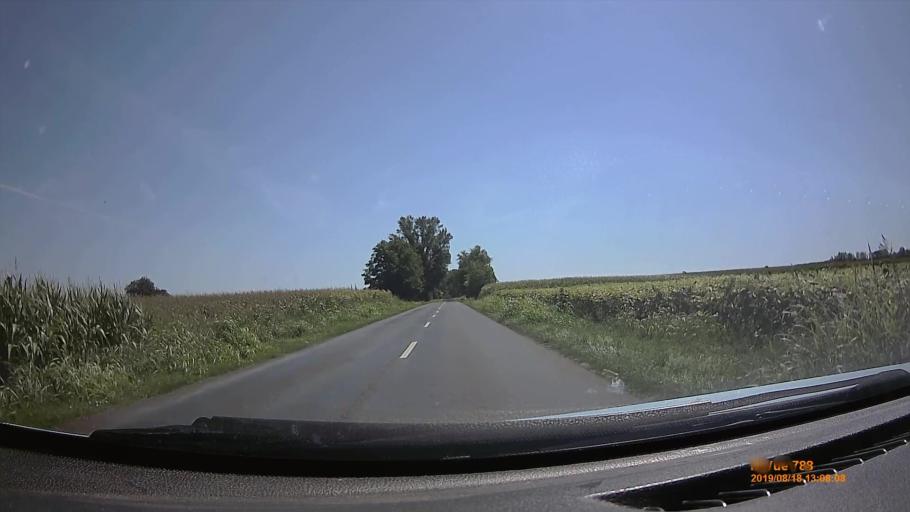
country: HU
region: Fejer
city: Kaloz
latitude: 46.9425
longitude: 18.4996
